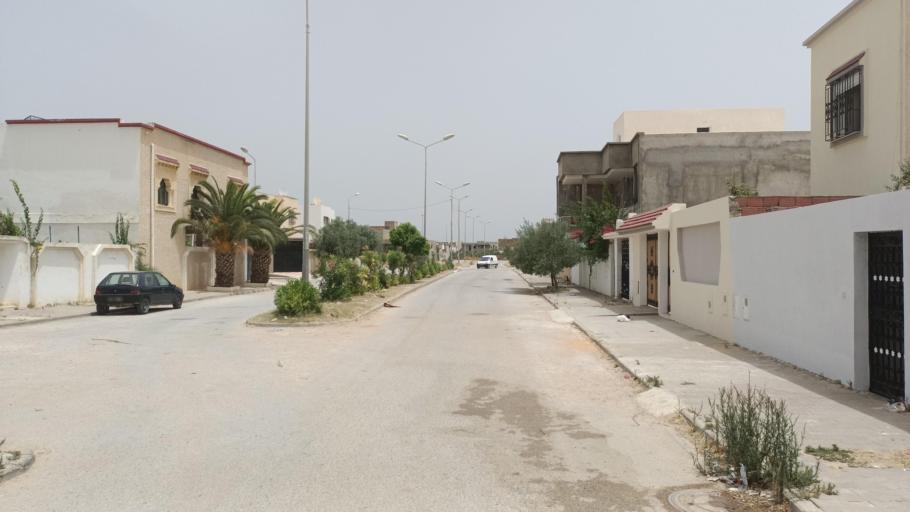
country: TN
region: Nabul
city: Manzil Bu Zalafah
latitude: 36.7037
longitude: 10.4892
